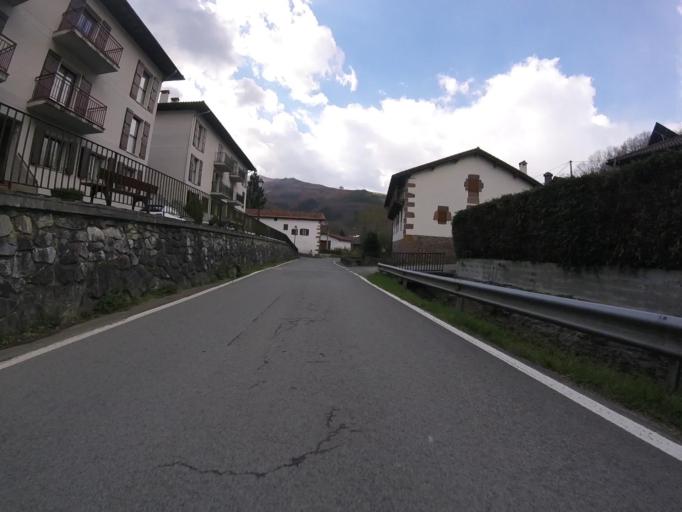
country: ES
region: Navarre
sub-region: Provincia de Navarra
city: Etxalar
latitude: 43.2377
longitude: -1.6341
